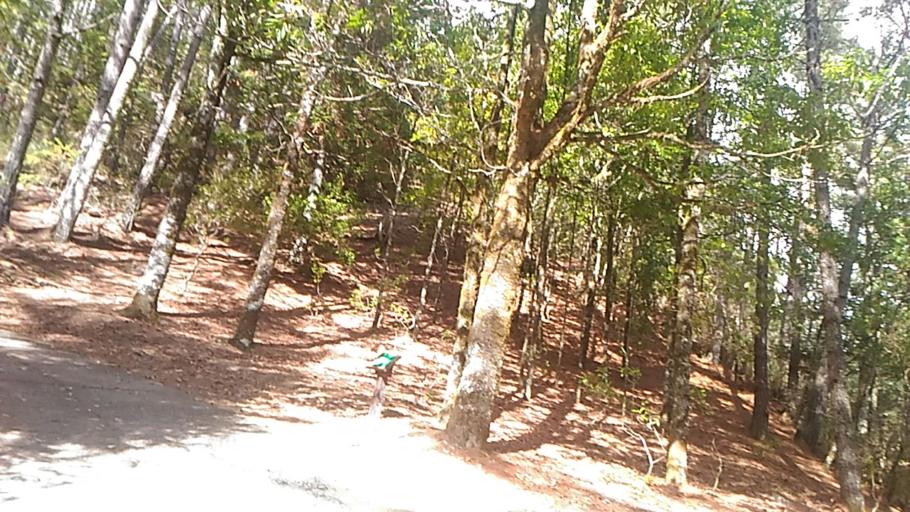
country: TW
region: Taiwan
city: Daxi
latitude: 24.4032
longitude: 121.3062
